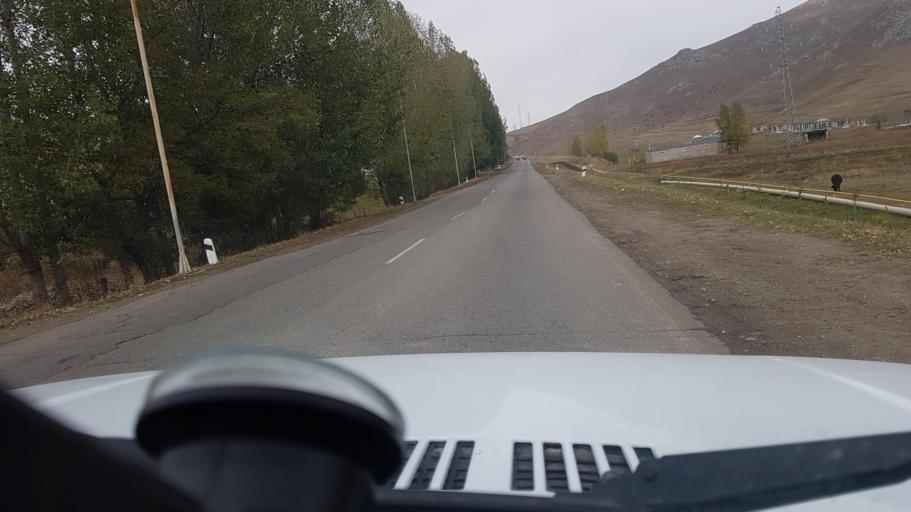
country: AZ
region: Gadabay Rayon
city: Ariqdam
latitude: 40.6082
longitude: 45.8126
